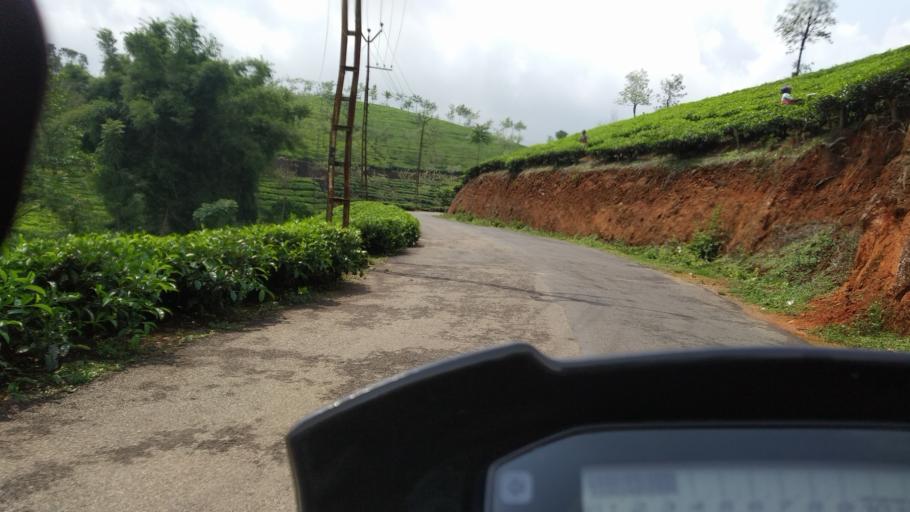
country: IN
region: Kerala
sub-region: Kottayam
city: Erattupetta
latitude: 9.6268
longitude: 76.9757
